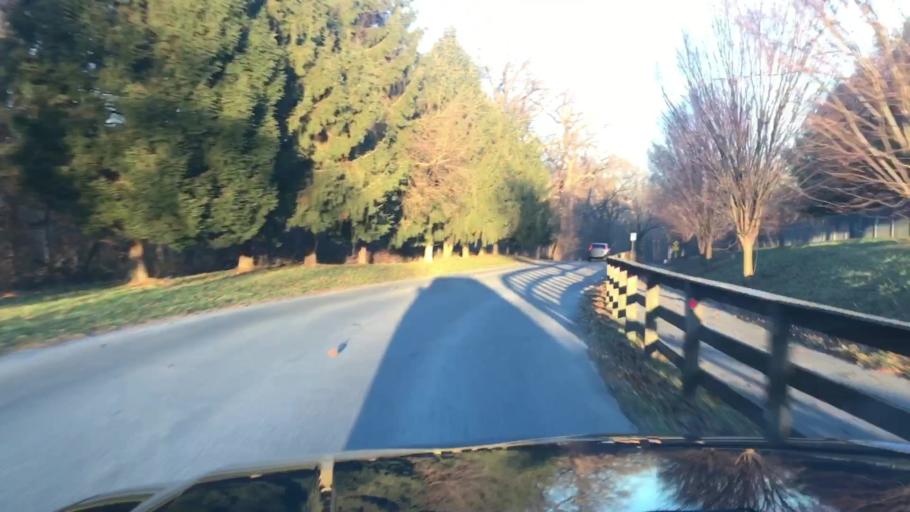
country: US
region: Pennsylvania
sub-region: Dauphin County
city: Harrisburg
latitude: 40.2806
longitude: -76.8714
